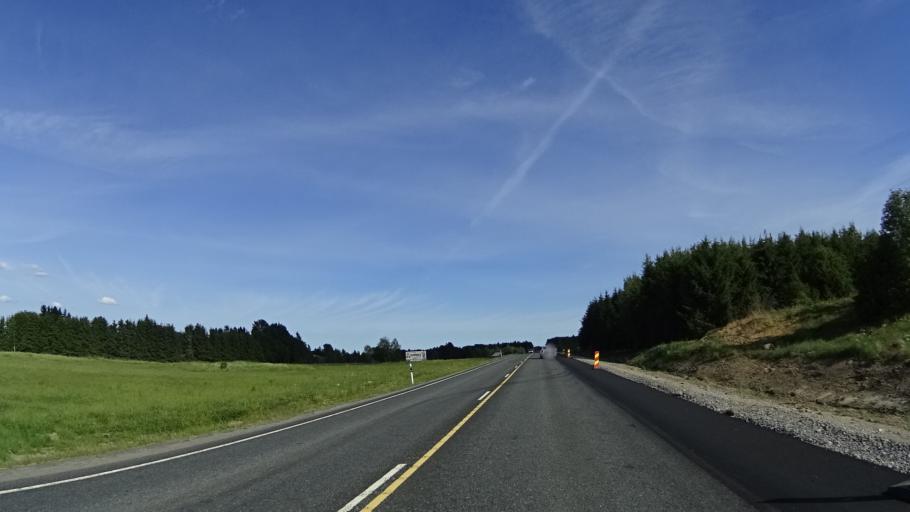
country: FI
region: Haeme
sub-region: Forssa
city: Tammela
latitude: 60.7599
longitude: 23.6973
